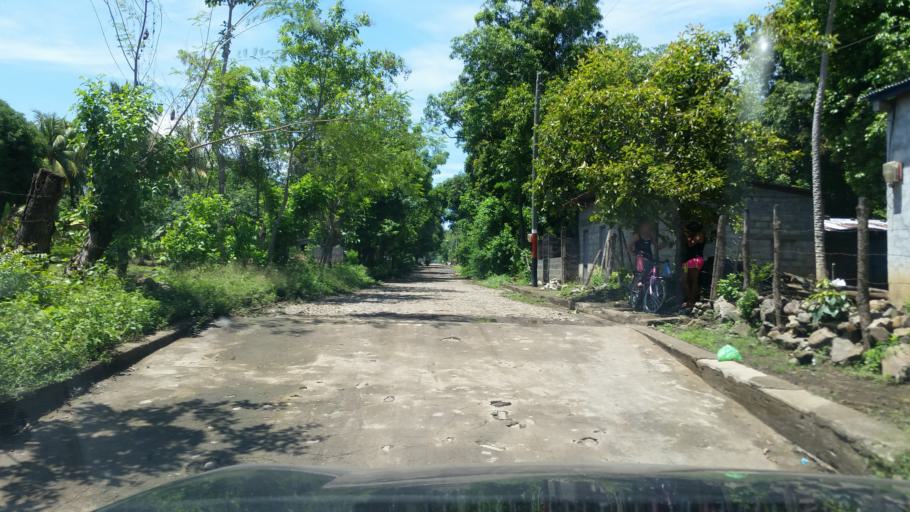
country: NI
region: Chinandega
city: Puerto Morazan
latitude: 12.7684
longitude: -87.1317
